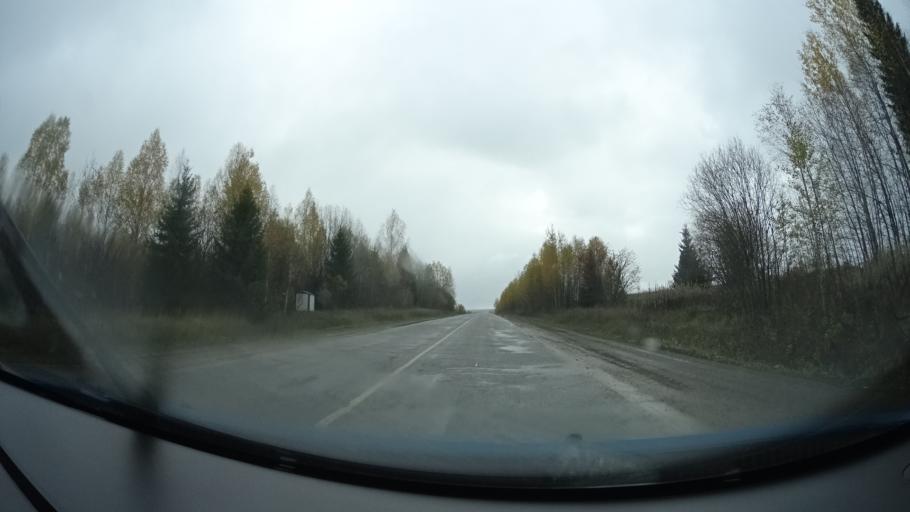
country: RU
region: Perm
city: Chernushka
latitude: 56.7577
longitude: 56.1431
